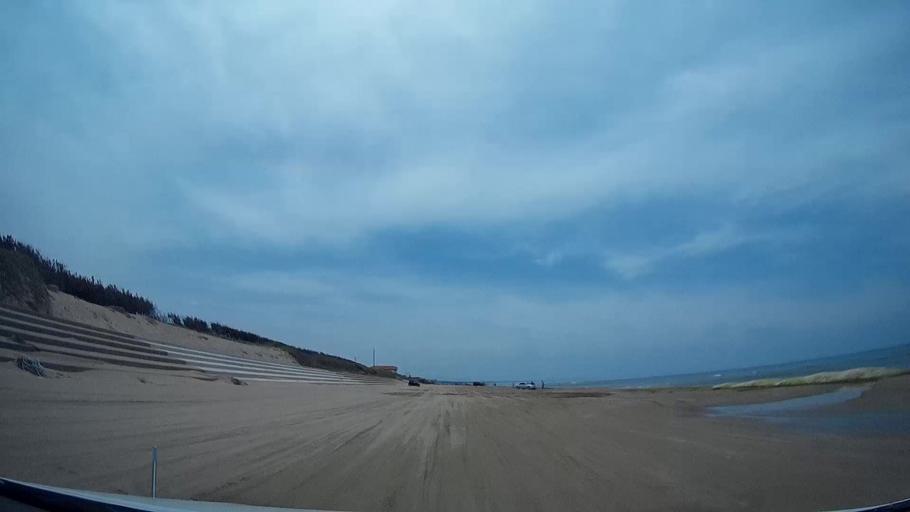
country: JP
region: Ishikawa
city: Hakui
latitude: 36.8975
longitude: 136.7667
